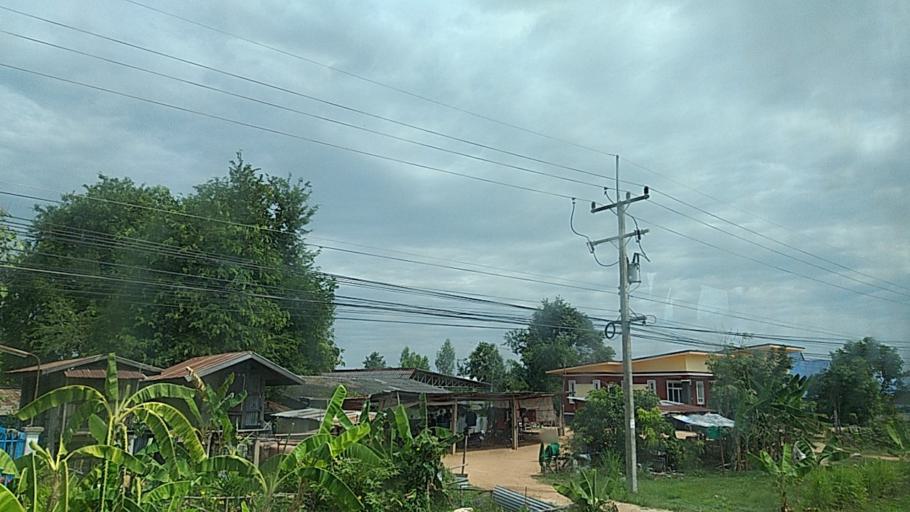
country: TH
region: Maha Sarakham
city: Chiang Yuen
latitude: 16.3430
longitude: 103.1518
